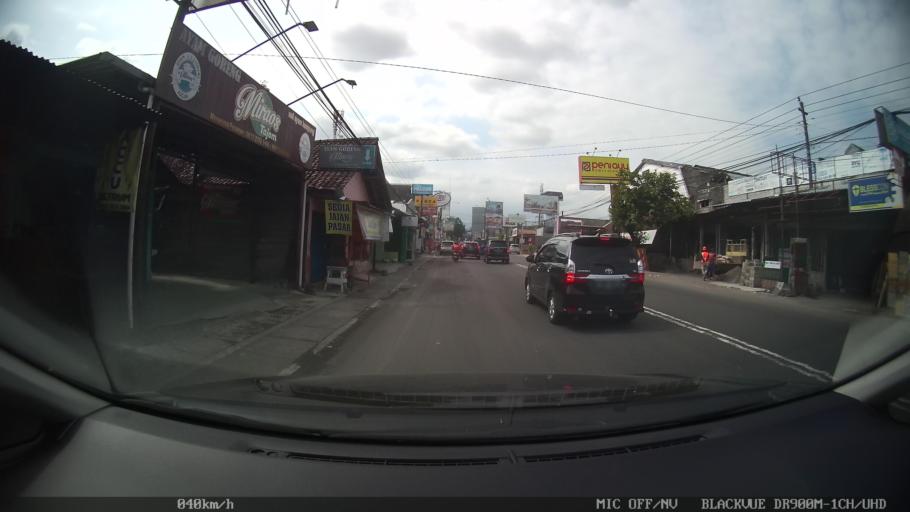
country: ID
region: Daerah Istimewa Yogyakarta
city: Depok
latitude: -7.7524
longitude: 110.4343
